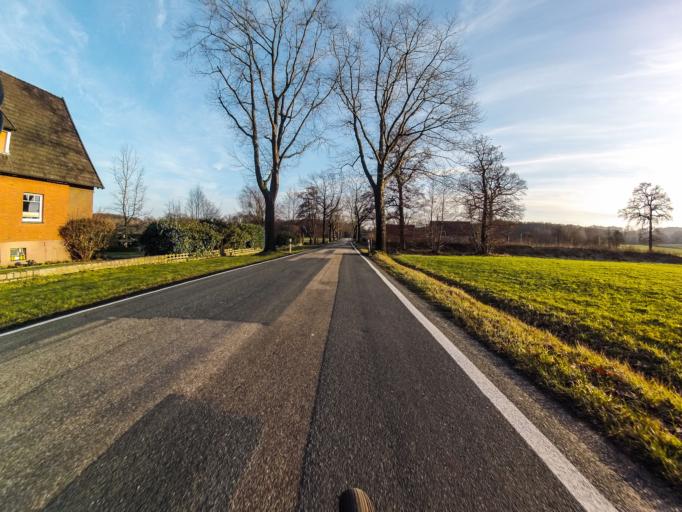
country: DE
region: North Rhine-Westphalia
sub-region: Regierungsbezirk Munster
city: Mettingen
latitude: 52.3008
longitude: 7.8185
